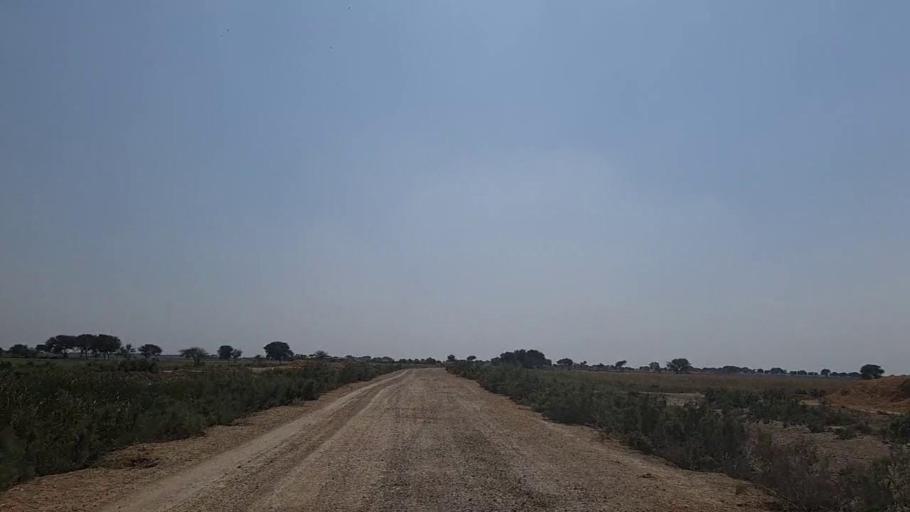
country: PK
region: Sindh
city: Mirpur Batoro
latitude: 24.5426
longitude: 68.3163
